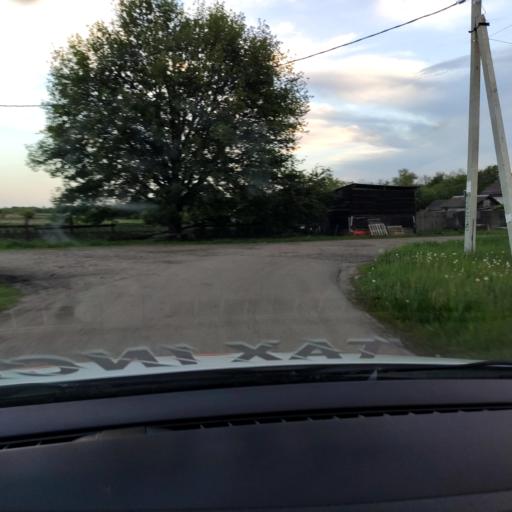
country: RU
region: Voronezj
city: Maslovka
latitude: 51.4381
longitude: 39.2328
